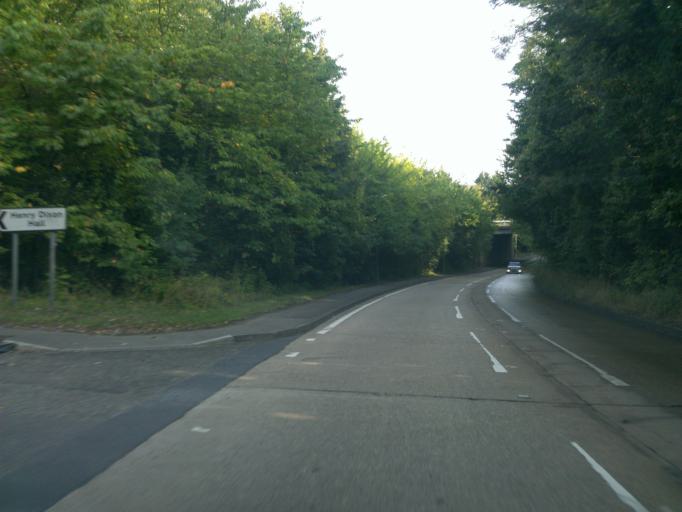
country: GB
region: England
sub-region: Essex
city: Witham
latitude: 51.8186
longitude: 0.6672
